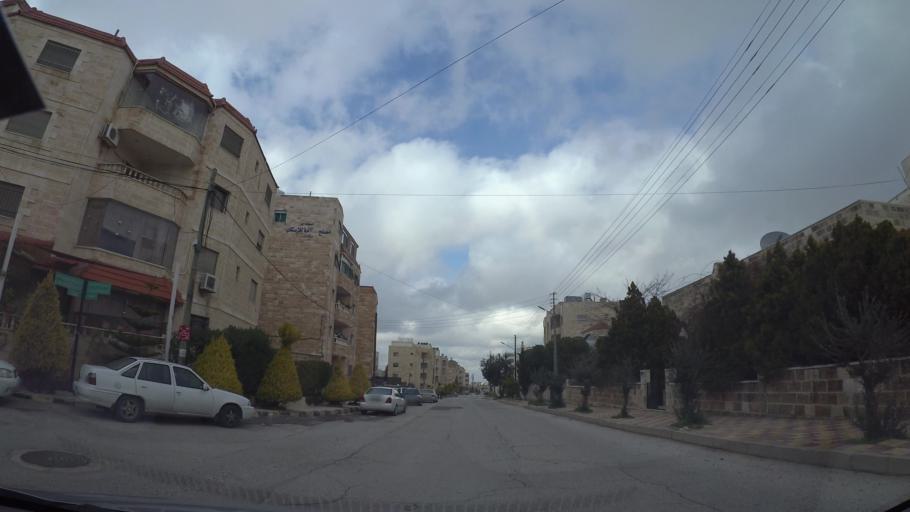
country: JO
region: Amman
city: Al Jubayhah
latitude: 32.0456
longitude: 35.9010
